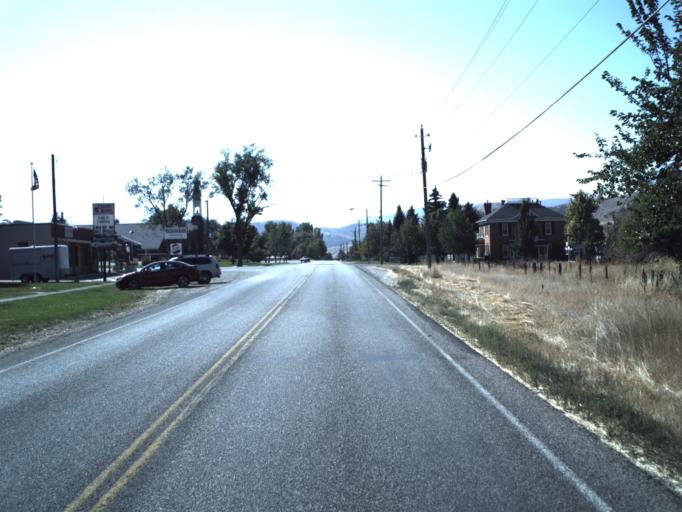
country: US
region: Utah
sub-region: Cache County
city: Hyrum
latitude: 41.5697
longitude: -111.8384
